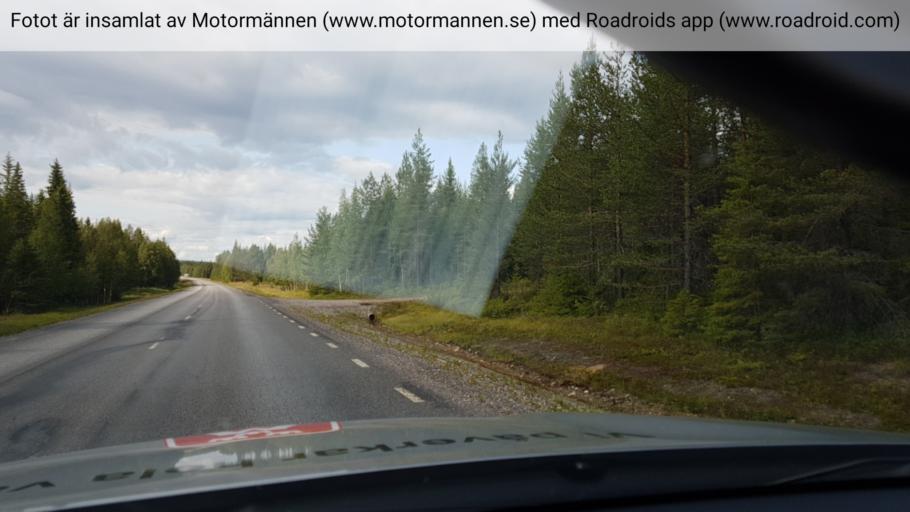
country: SE
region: Norrbotten
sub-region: Arvidsjaurs Kommun
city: Arvidsjaur
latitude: 65.5891
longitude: 19.4617
